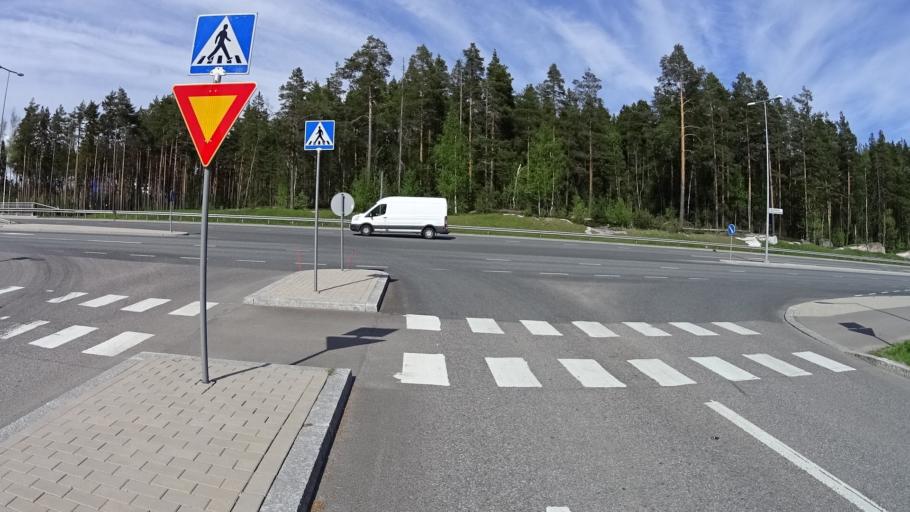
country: FI
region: Uusimaa
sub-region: Helsinki
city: Vantaa
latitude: 60.3004
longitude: 24.9652
